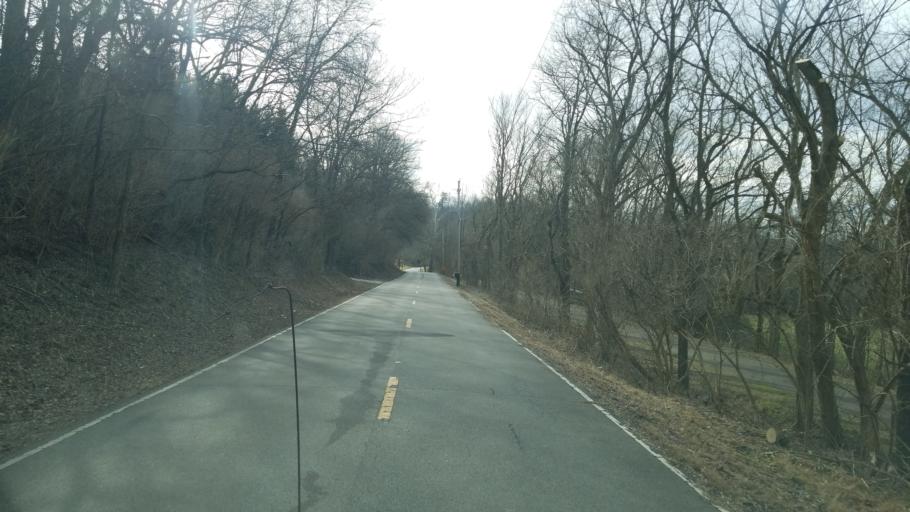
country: US
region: Ohio
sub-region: Warren County
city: Morrow
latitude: 39.4368
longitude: -84.1011
